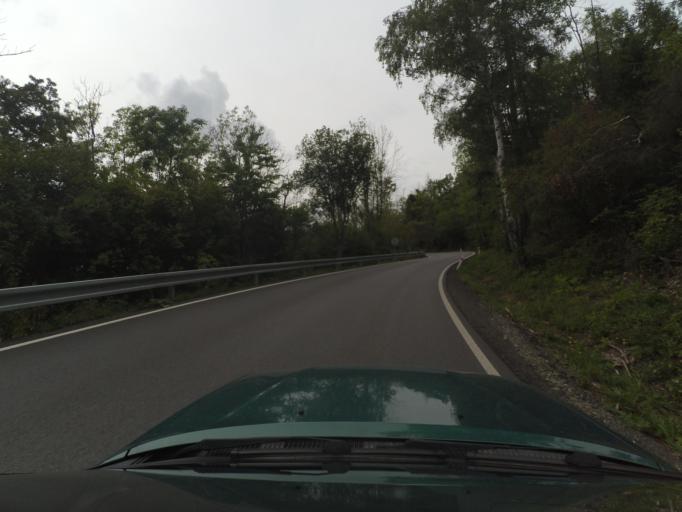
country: CZ
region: Central Bohemia
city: Revnicov
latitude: 50.1995
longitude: 13.7536
